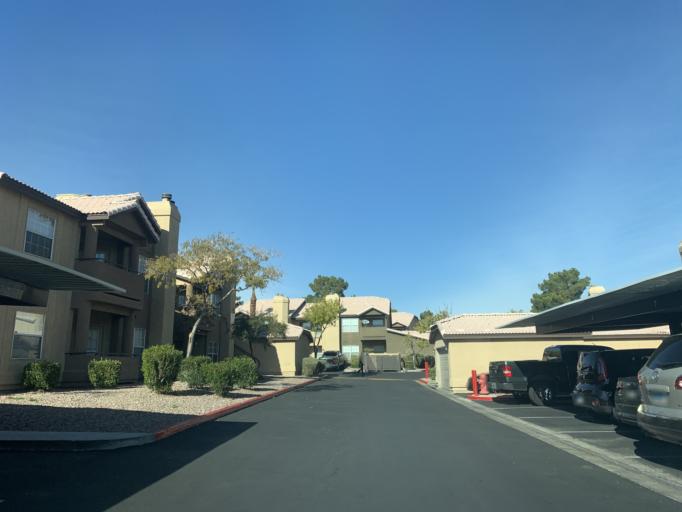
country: US
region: Nevada
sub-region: Clark County
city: Summerlin South
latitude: 36.1286
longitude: -115.2906
